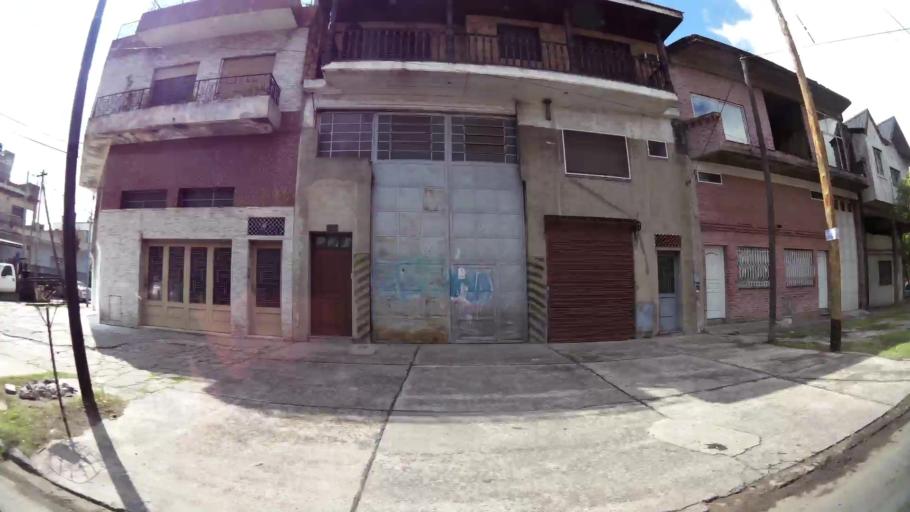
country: AR
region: Buenos Aires
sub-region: Partido de Lanus
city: Lanus
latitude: -34.6844
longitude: -58.4082
